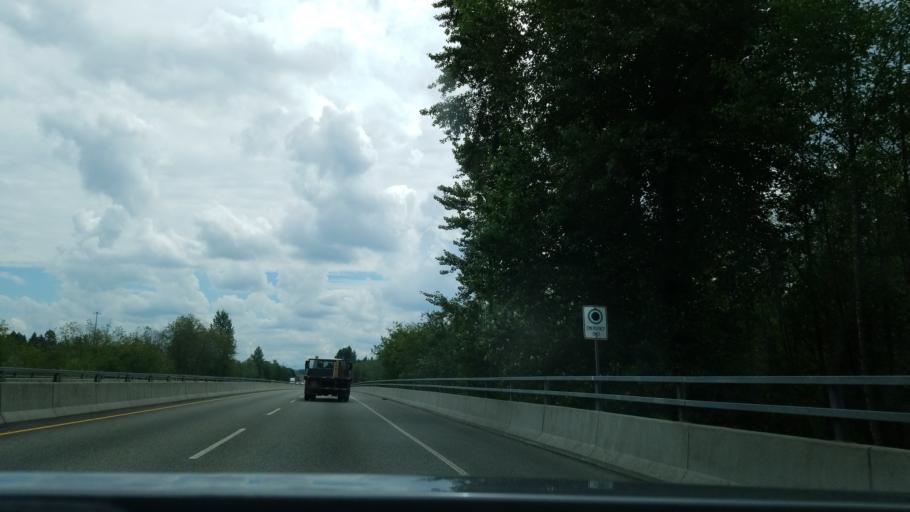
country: CA
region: British Columbia
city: Pitt Meadows
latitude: 49.2030
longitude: -122.7575
